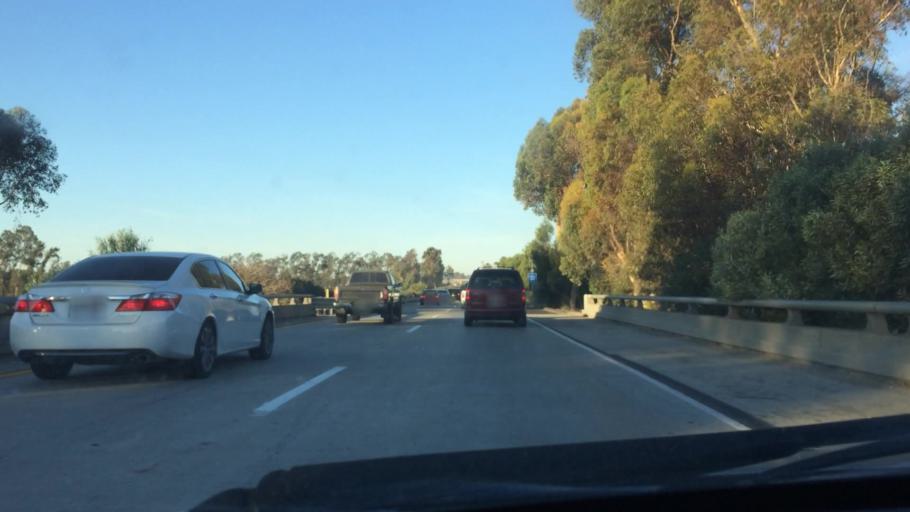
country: US
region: California
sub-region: Ventura County
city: Saticoy
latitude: 34.3134
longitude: -119.1167
